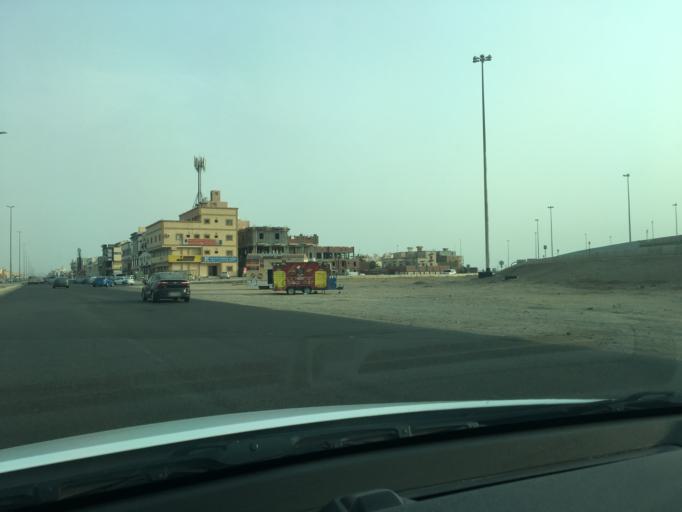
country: SA
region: Makkah
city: Jeddah
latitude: 21.7617
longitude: 39.1833
